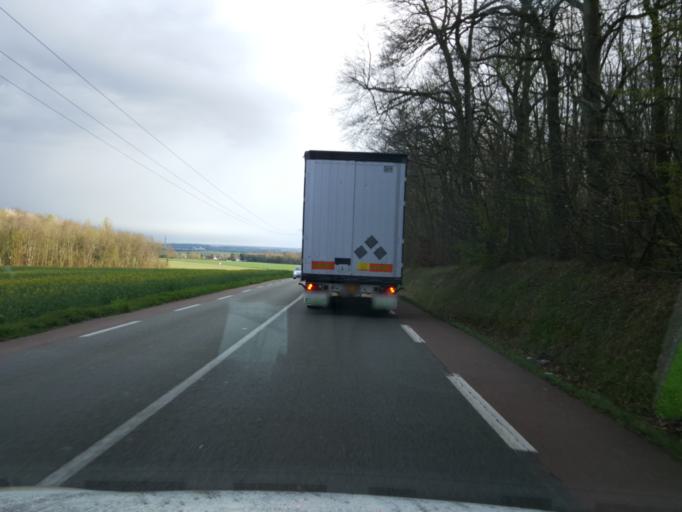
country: FR
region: Ile-de-France
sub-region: Departement des Yvelines
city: Follainville-Dennemont
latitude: 49.0415
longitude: 1.7507
